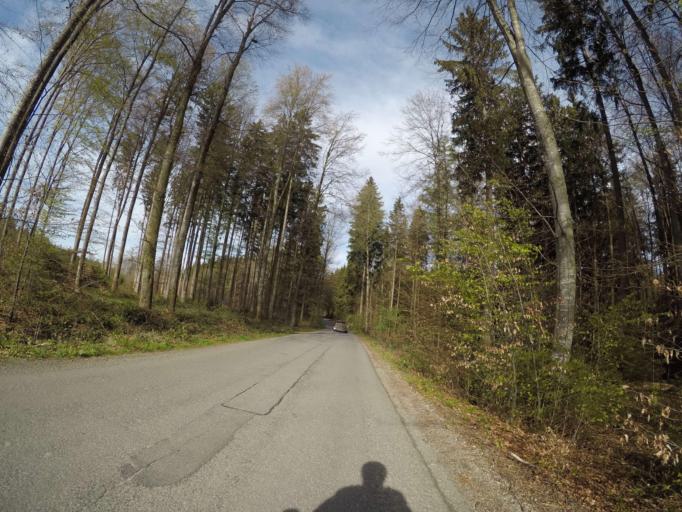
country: DE
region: Baden-Wuerttemberg
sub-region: Tuebingen Region
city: Allmannsweiler
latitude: 47.9990
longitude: 9.6039
